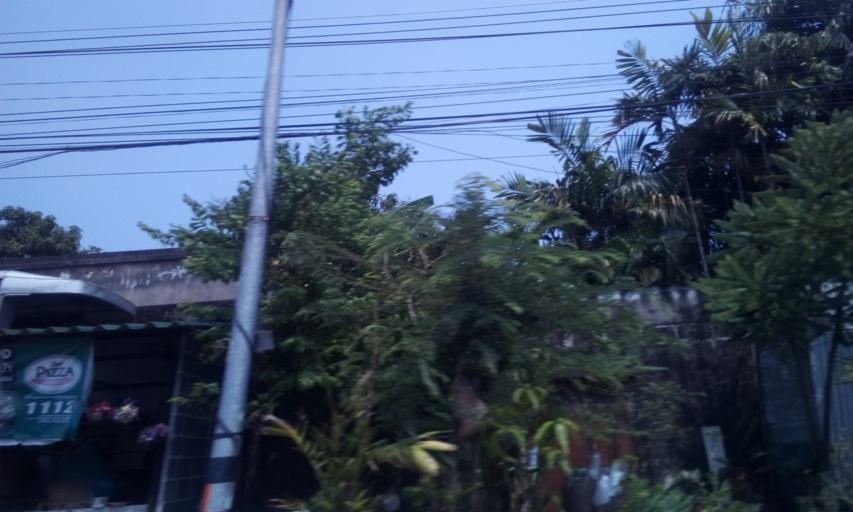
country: TH
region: Chon Buri
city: Phanat Nikhom
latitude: 13.4371
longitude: 101.1798
